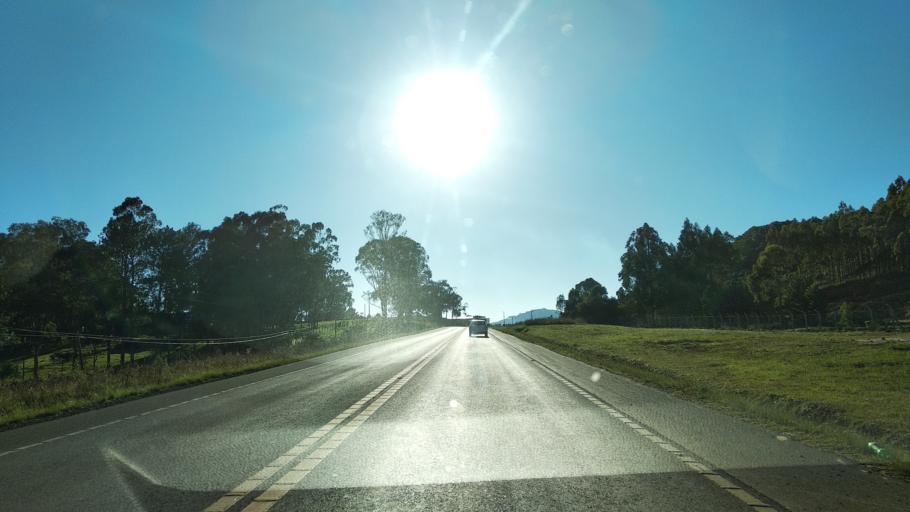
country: BR
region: Santa Catarina
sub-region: Lages
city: Lages
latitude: -27.7933
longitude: -50.3767
